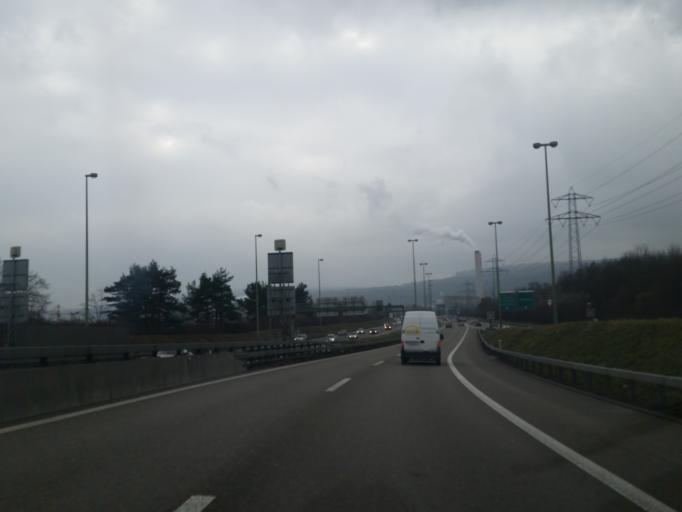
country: CH
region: Zurich
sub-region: Bezirk Buelach
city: Grossacker/Opfikon
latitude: 47.4219
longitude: 8.5742
